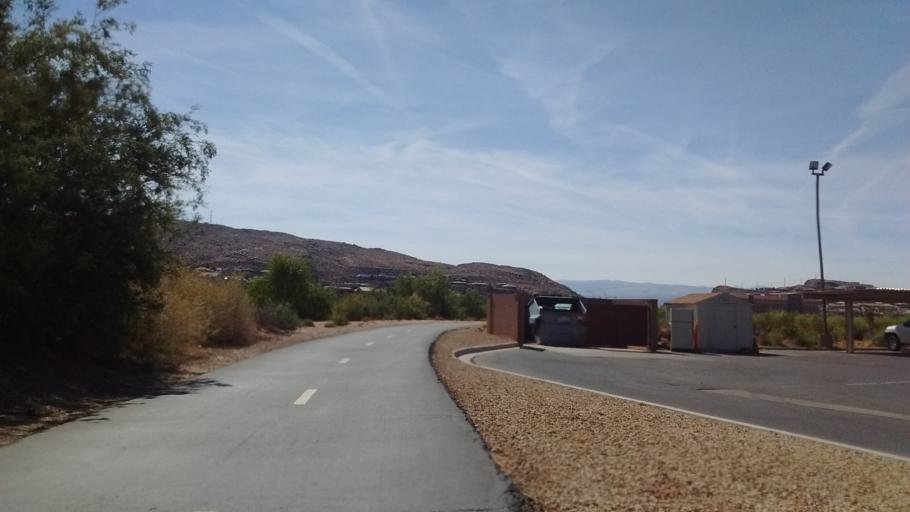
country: US
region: Utah
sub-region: Washington County
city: Saint George
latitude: 37.0817
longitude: -113.5746
